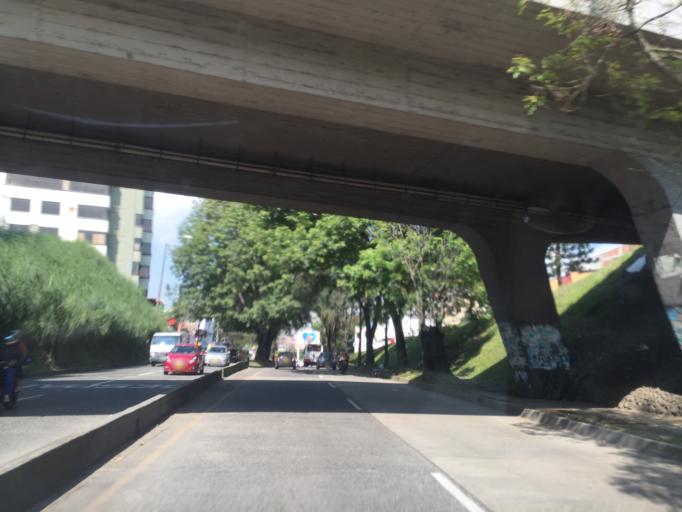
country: CO
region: Risaralda
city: Pereira
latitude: 4.8048
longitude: -75.6969
